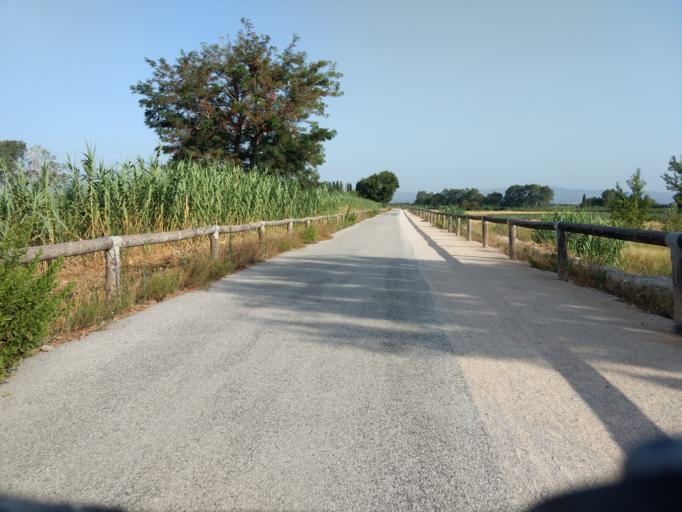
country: FR
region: Languedoc-Roussillon
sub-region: Departement des Pyrenees-Orientales
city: Claira
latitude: 42.7570
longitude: 2.9371
